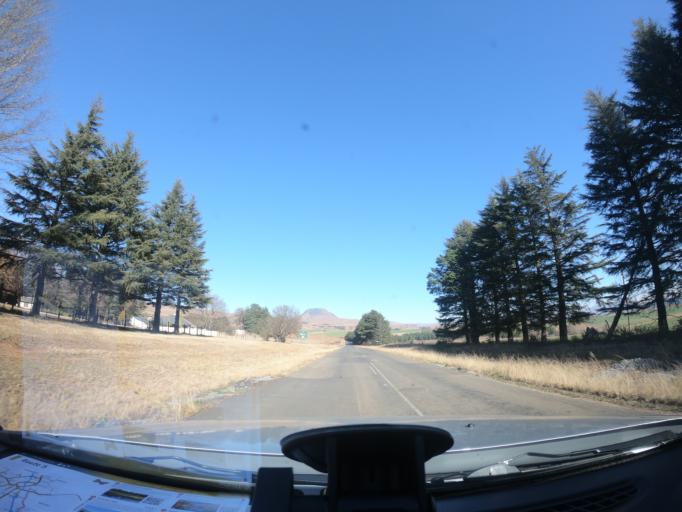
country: ZA
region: KwaZulu-Natal
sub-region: uMgungundlovu District Municipality
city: Mooirivier
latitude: -29.3287
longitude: 29.8241
